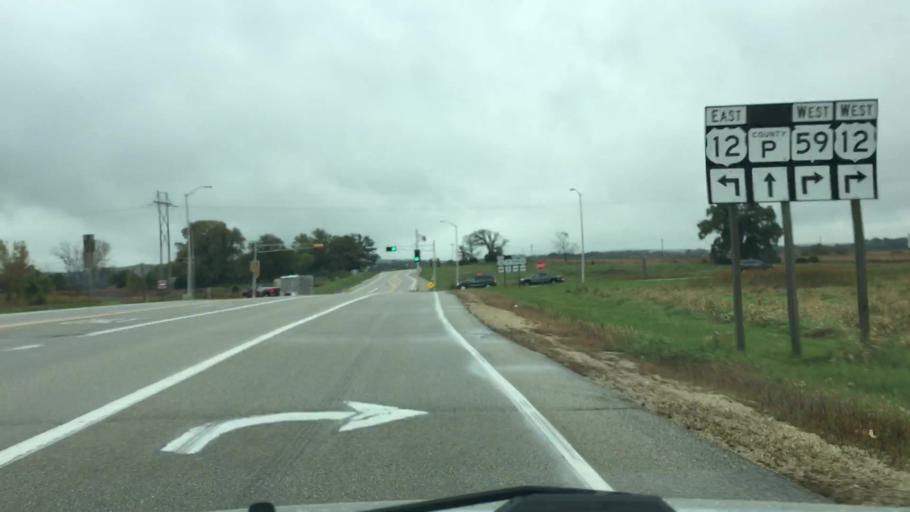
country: US
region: Wisconsin
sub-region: Walworth County
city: Whitewater
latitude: 42.8203
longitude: -88.7005
